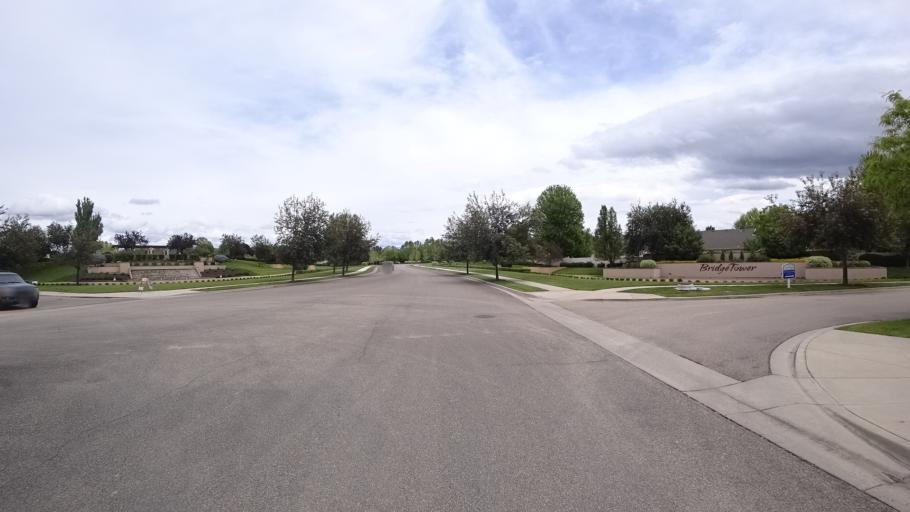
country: US
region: Idaho
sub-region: Ada County
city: Meridian
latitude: 43.6436
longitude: -116.4324
